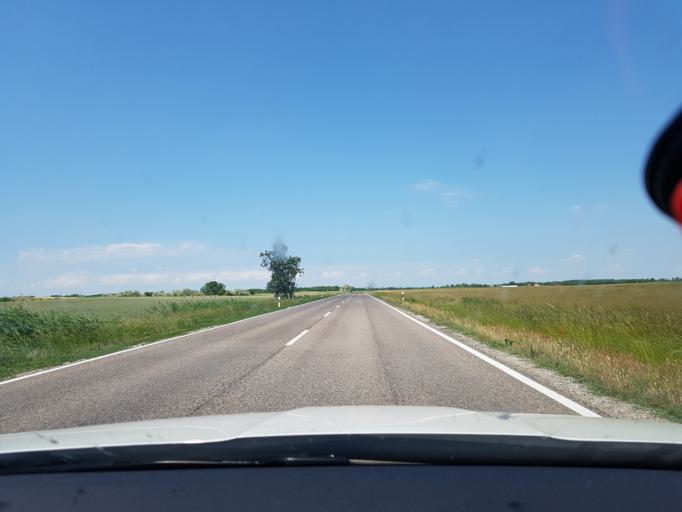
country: HU
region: Hajdu-Bihar
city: Egyek
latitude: 47.5756
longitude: 20.8569
